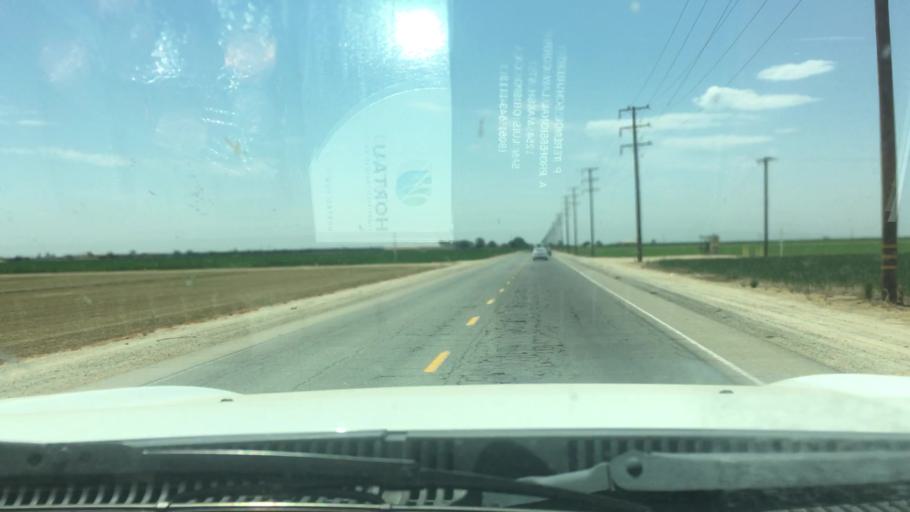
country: US
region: California
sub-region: Tulare County
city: Tipton
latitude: 36.0657
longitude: -119.2761
